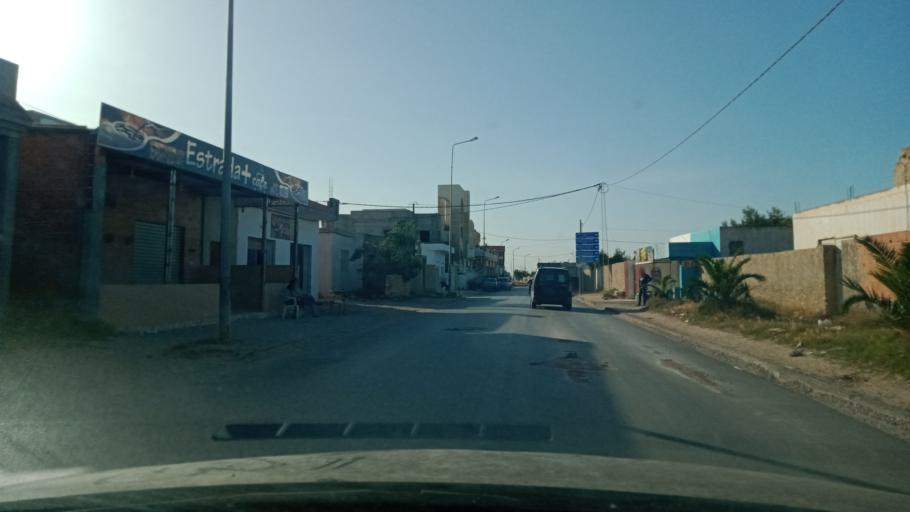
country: TN
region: Safaqis
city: Al Qarmadah
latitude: 34.8203
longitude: 10.7417
